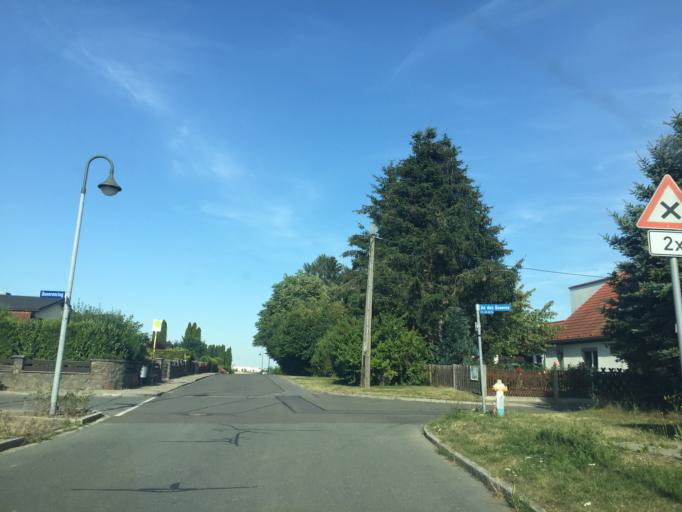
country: DE
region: Thuringia
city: Schmolln
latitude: 50.8859
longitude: 12.3619
